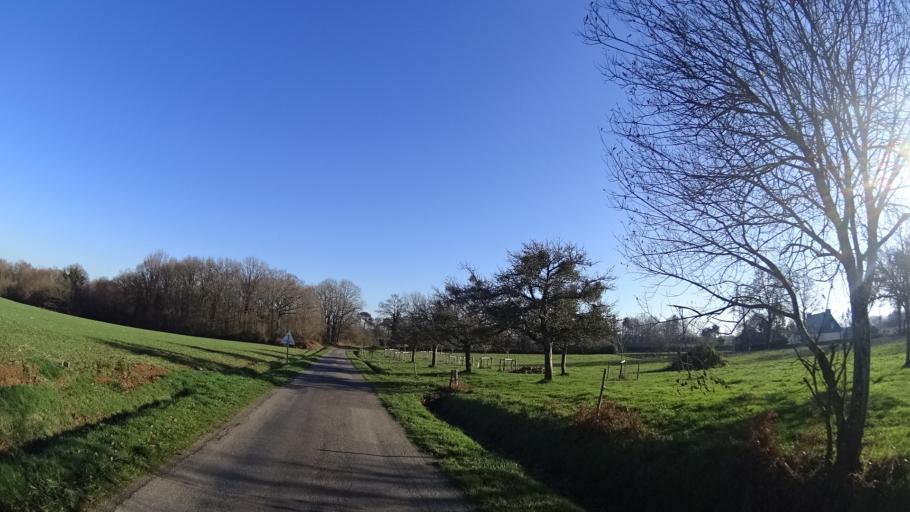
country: FR
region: Brittany
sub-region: Departement du Morbihan
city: Saint-Jean-la-Poterie
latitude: 47.6480
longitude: -2.1355
